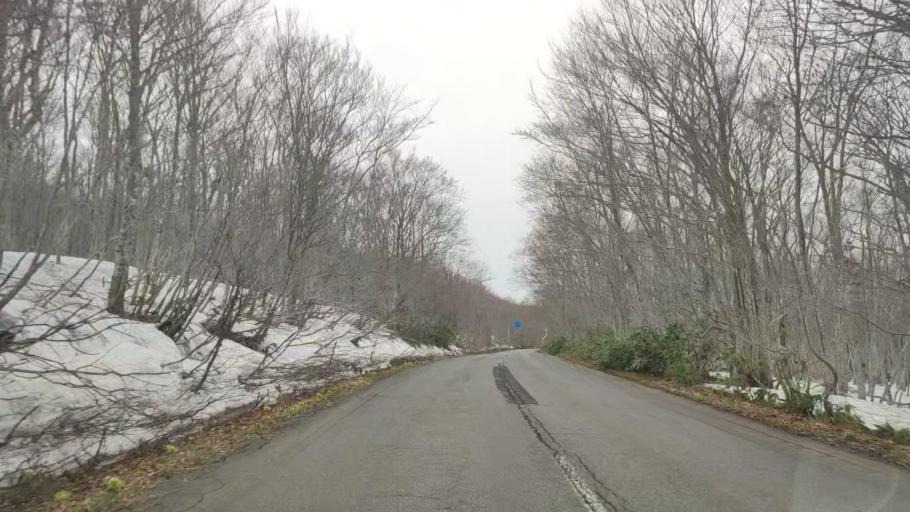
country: JP
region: Aomori
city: Aomori Shi
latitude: 40.6475
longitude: 140.9445
